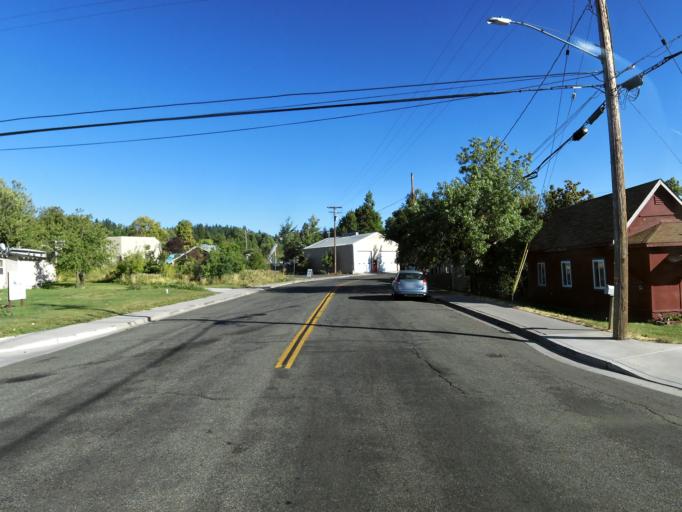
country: US
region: California
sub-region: Siskiyou County
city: Mount Shasta
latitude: 41.3129
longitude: -122.3153
